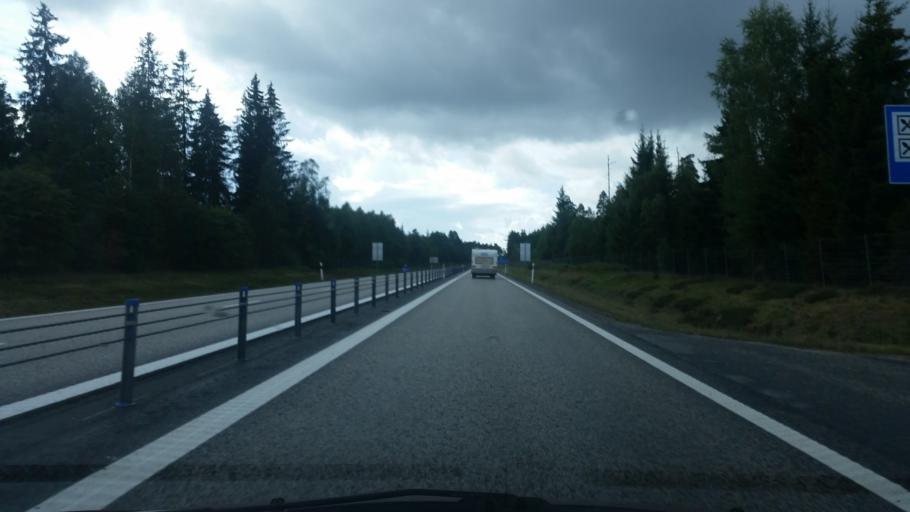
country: SE
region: Joenkoeping
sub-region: Gislaveds Kommun
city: Gislaved
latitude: 57.3347
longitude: 13.5485
